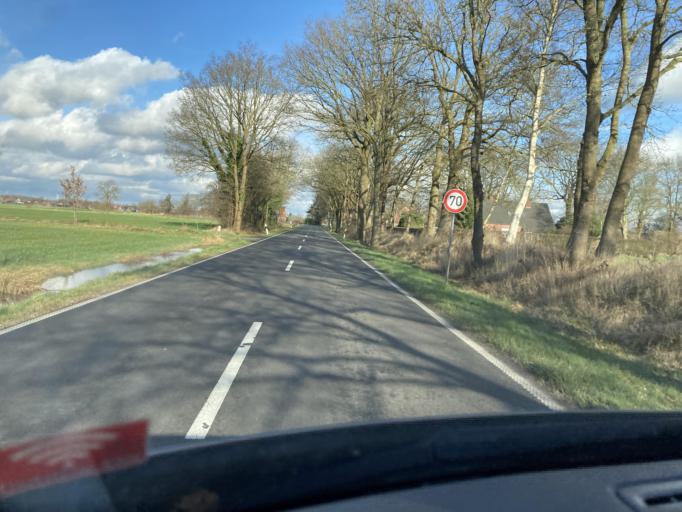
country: DE
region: Lower Saxony
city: Schwerinsdorf
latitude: 53.2715
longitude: 7.7117
